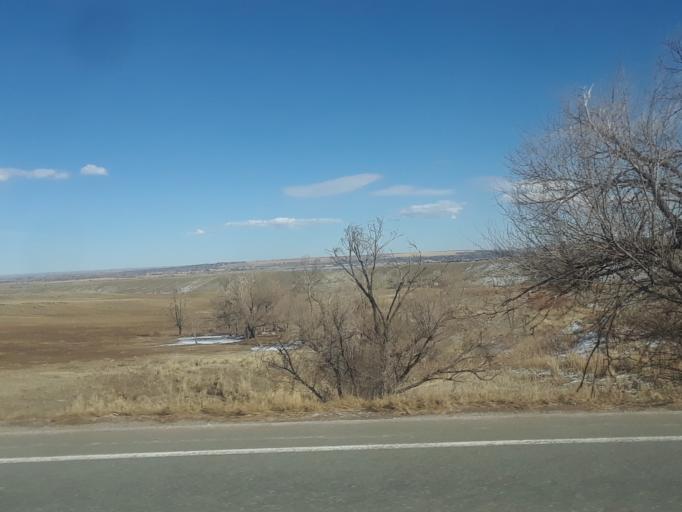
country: US
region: Colorado
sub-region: Boulder County
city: Boulder
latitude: 40.0817
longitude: -105.2822
